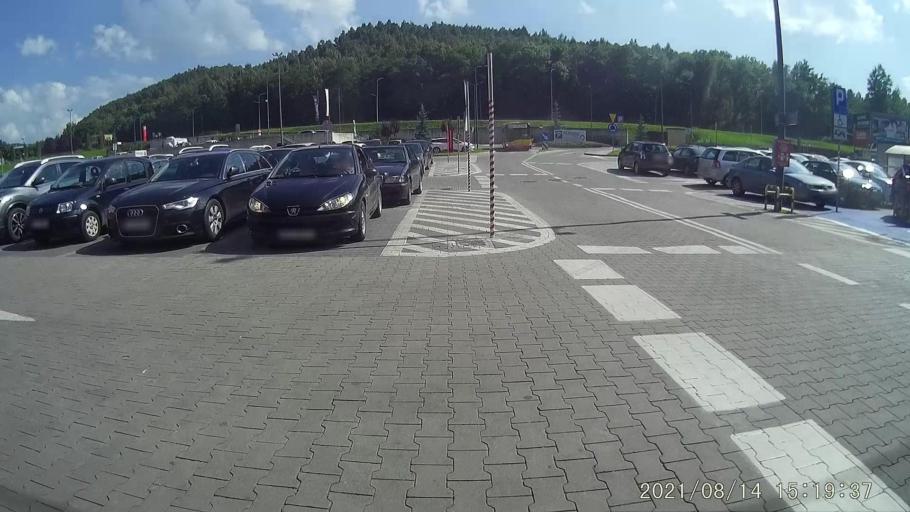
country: PL
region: Lower Silesian Voivodeship
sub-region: Powiat walbrzyski
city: Walbrzych
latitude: 50.7662
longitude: 16.2637
